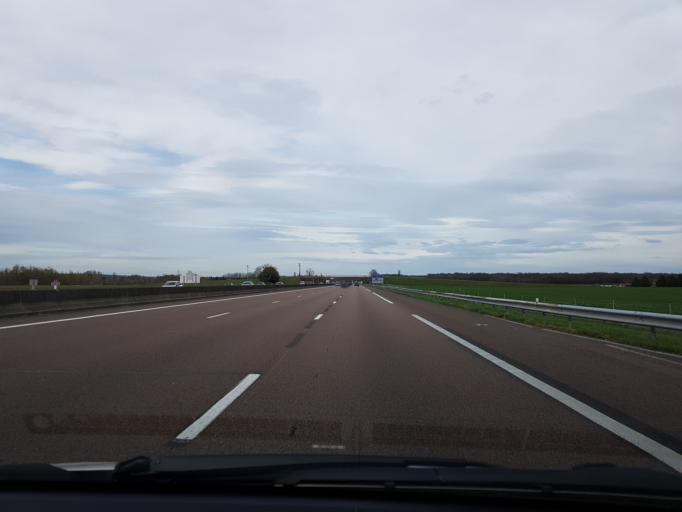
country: FR
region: Bourgogne
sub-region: Departement de Saone-et-Loire
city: Demigny
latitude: 46.9469
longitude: 4.8303
